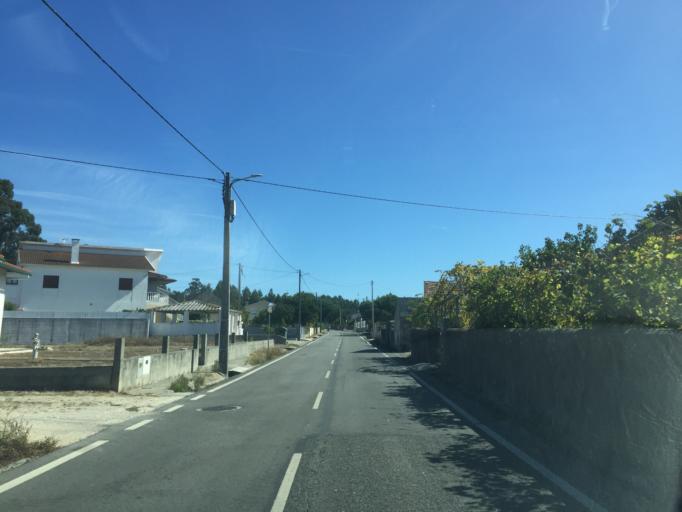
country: PT
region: Coimbra
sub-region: Figueira da Foz
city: Alhadas
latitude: 40.2204
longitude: -8.8181
